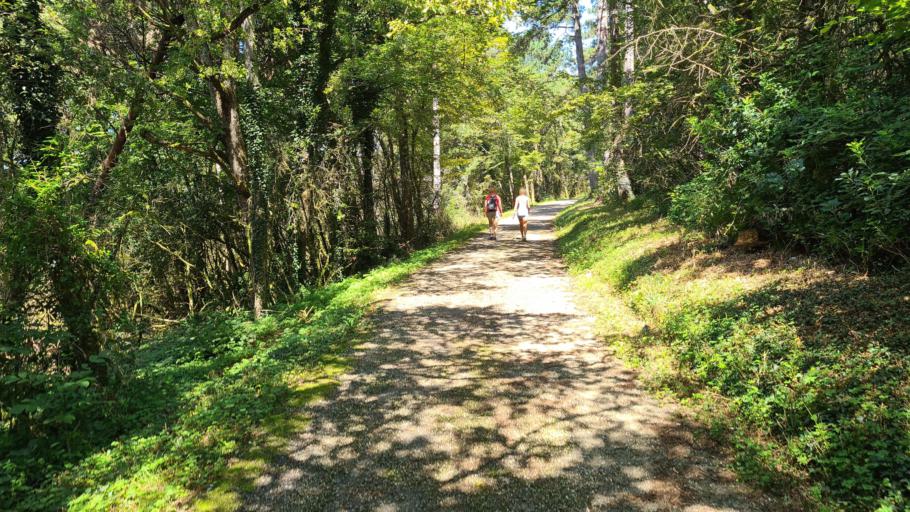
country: FR
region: Rhone-Alpes
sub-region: Departement de la Savoie
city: Brison-Saint-Innocent
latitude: 45.7117
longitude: 5.8974
